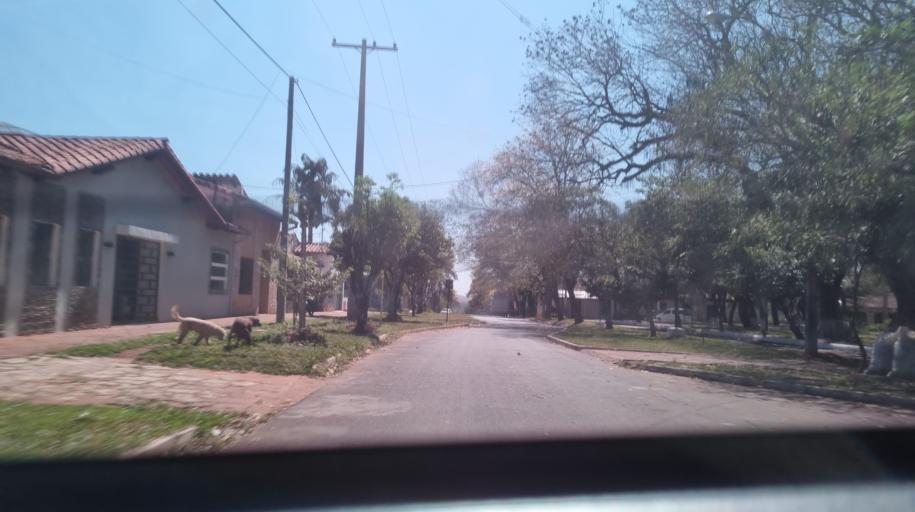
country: PY
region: Misiones
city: San Juan Bautista
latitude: -26.6675
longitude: -57.1471
